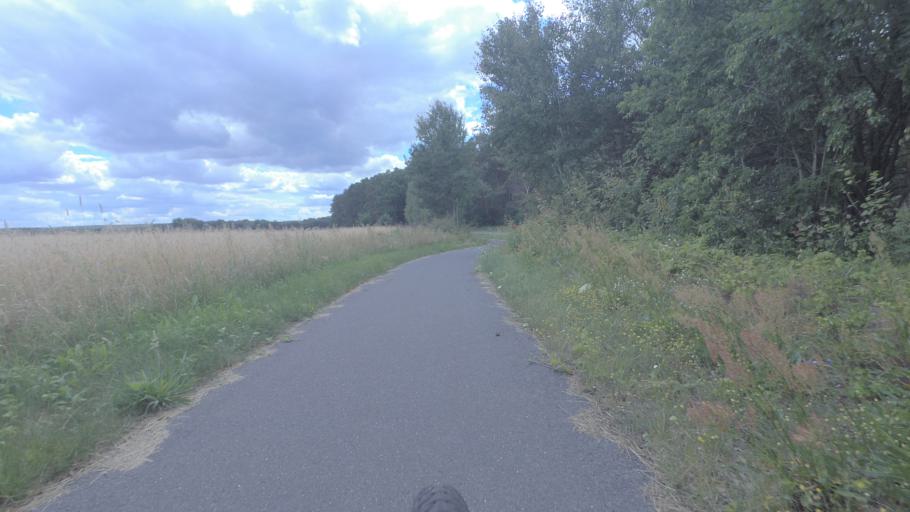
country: DE
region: Brandenburg
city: Luckenwalde
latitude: 52.1831
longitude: 13.1231
